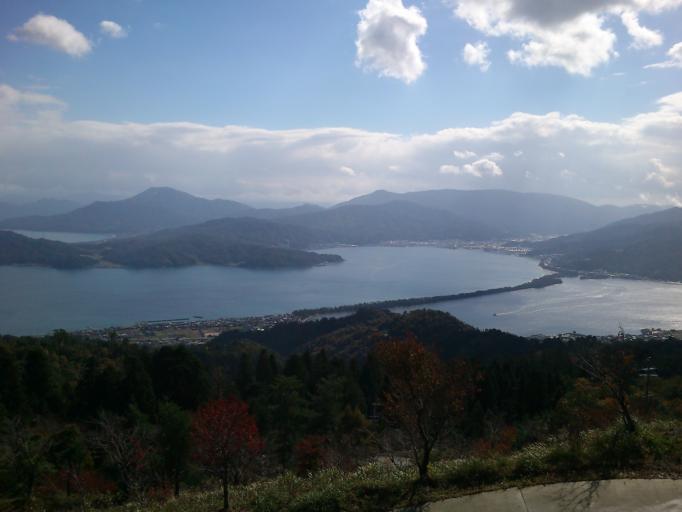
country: JP
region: Kyoto
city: Miyazu
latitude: 35.6011
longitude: 135.1879
